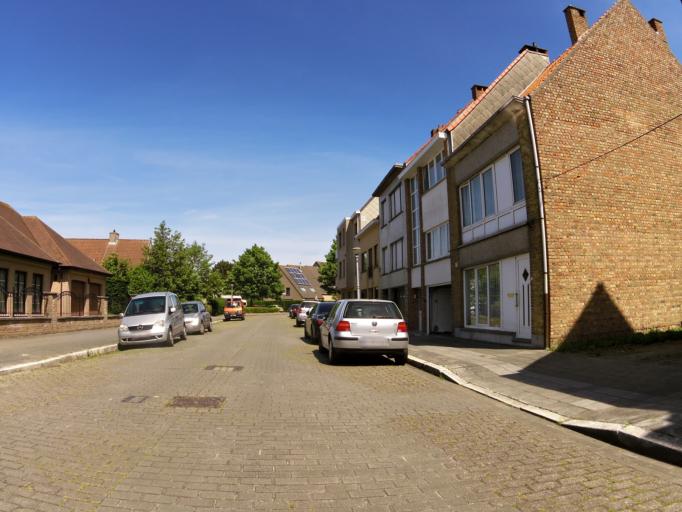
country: BE
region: Flanders
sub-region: Provincie West-Vlaanderen
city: Ostend
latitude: 51.2133
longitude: 2.8966
